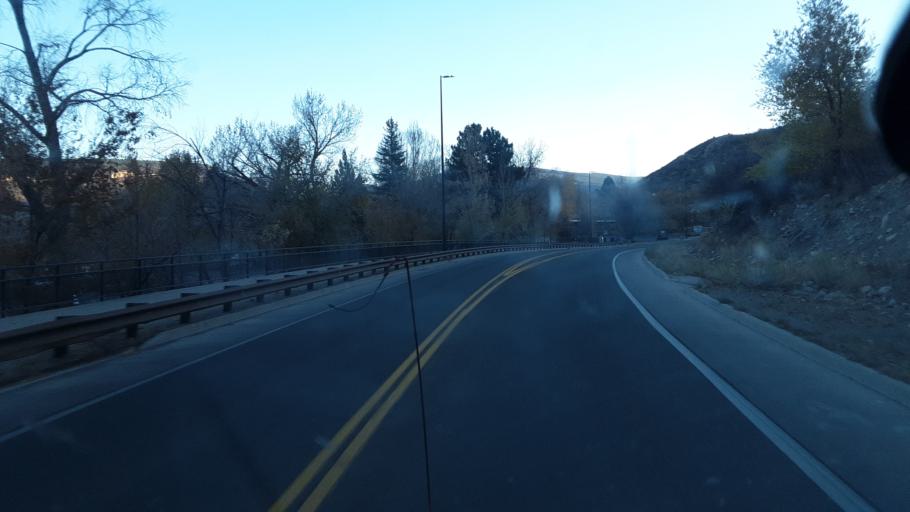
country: US
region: Colorado
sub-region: La Plata County
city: Durango
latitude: 37.2819
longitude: -107.8717
